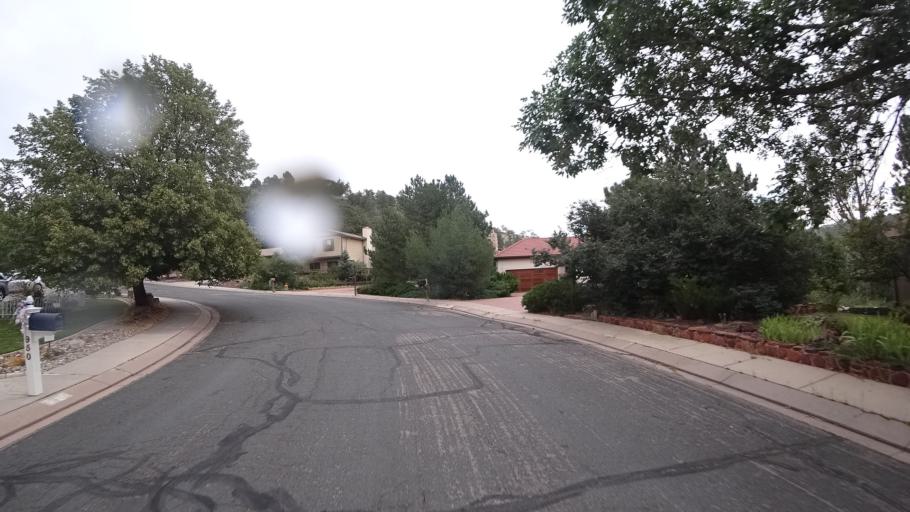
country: US
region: Colorado
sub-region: El Paso County
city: Colorado Springs
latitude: 38.9193
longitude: -104.8090
